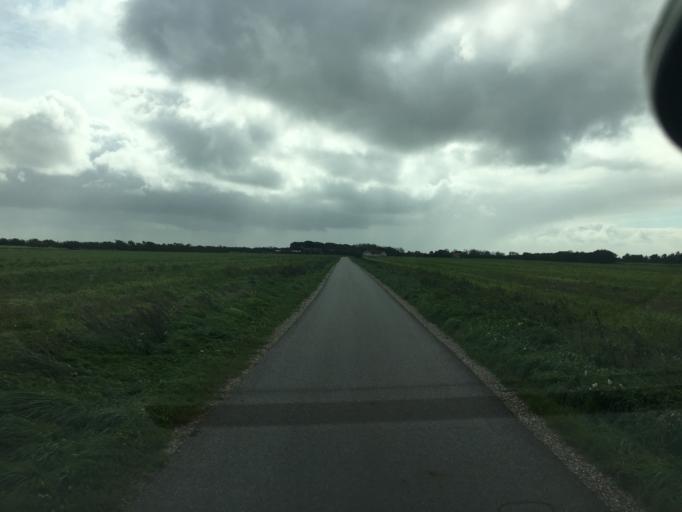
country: DK
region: South Denmark
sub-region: Tonder Kommune
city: Sherrebek
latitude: 55.0877
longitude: 8.8124
